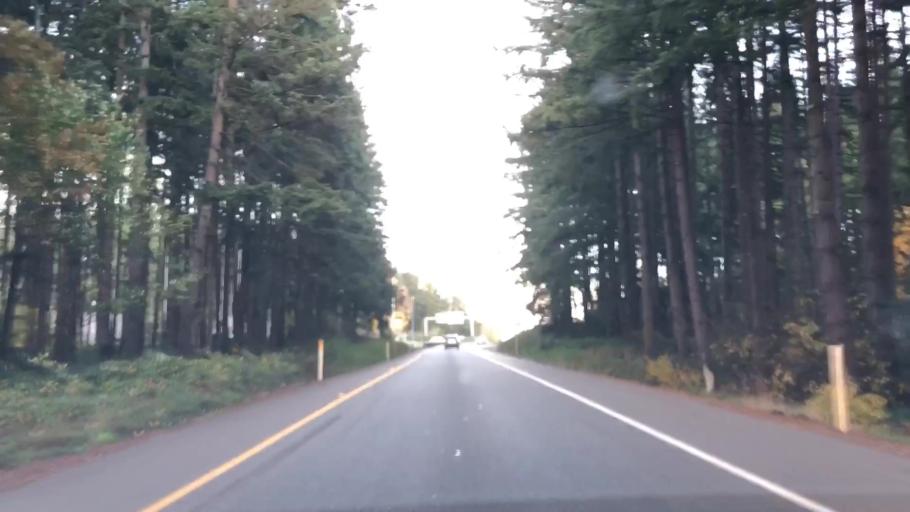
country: US
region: Washington
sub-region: King County
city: Lakeland South
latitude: 47.2884
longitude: -122.3042
